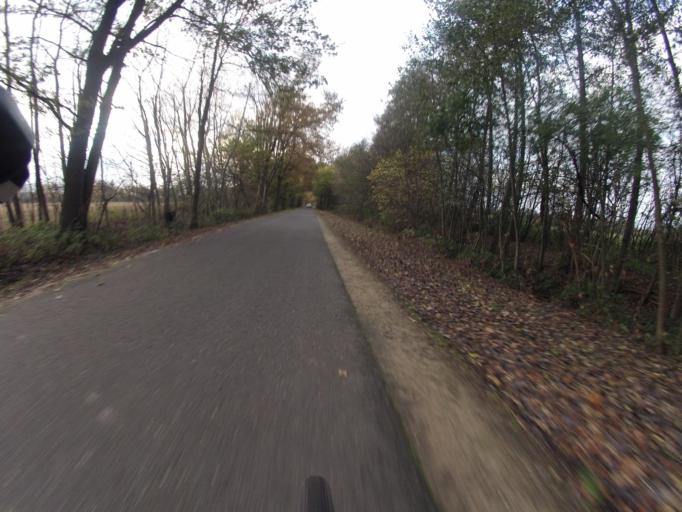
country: DE
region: North Rhine-Westphalia
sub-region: Regierungsbezirk Munster
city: Horstel
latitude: 52.2635
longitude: 7.5609
